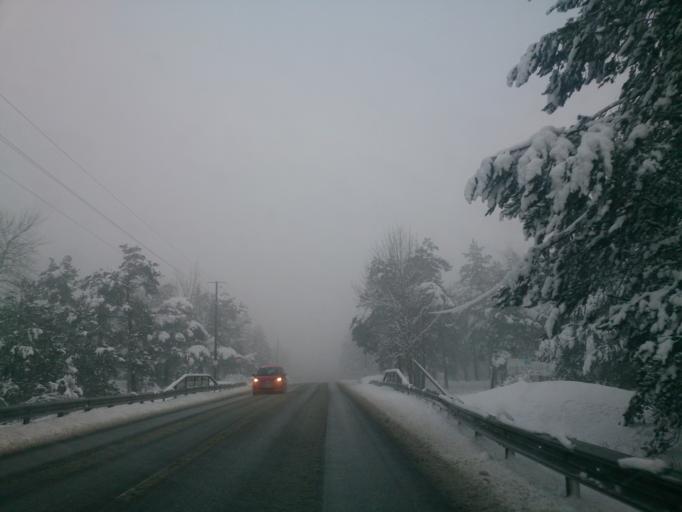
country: SE
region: Stockholm
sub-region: Varmdo Kommun
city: Holo
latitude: 59.2982
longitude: 18.6704
